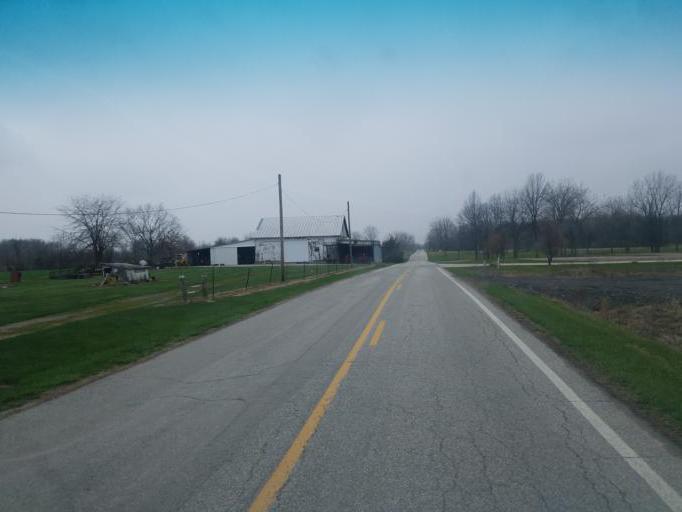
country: US
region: Ohio
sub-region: Delaware County
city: Delaware
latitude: 40.3796
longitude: -83.0763
